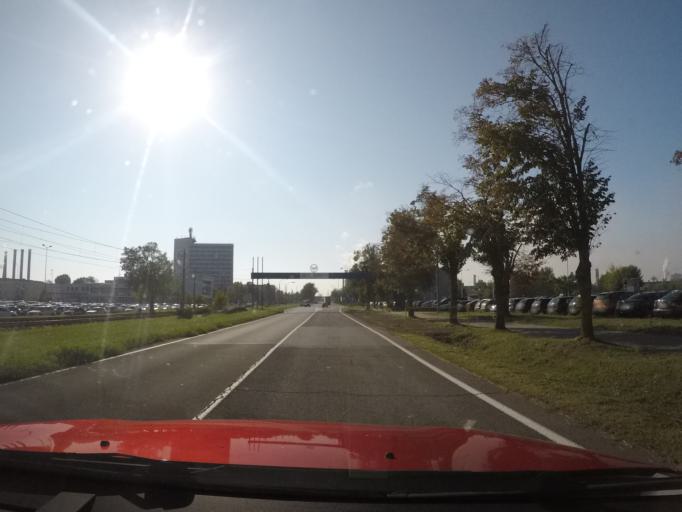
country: SK
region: Kosicky
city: Kosice
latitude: 48.6250
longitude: 21.1882
